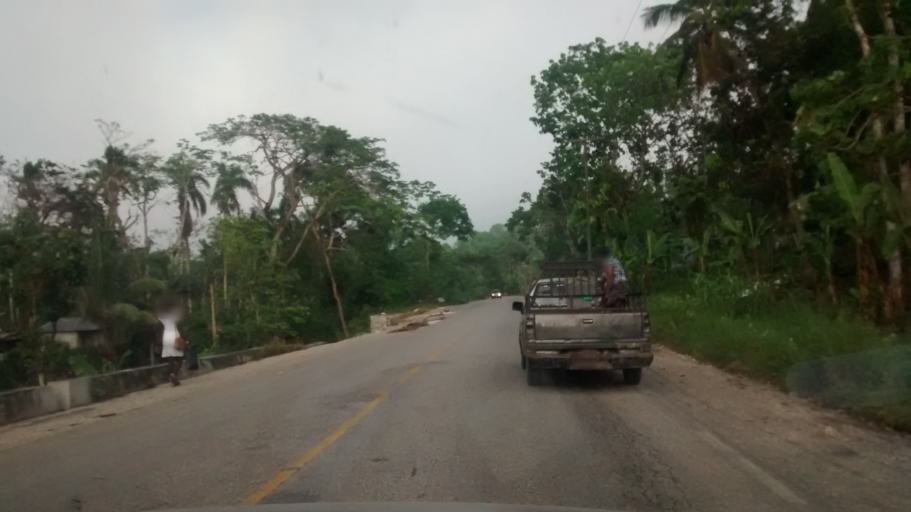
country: HT
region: Grandans
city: Petite Riviere de Nippes
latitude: 18.3620
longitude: -73.2170
